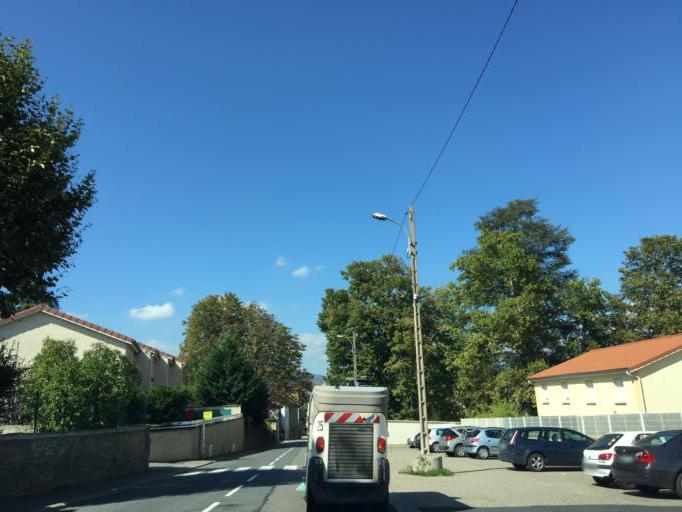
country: FR
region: Rhone-Alpes
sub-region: Departement de la Loire
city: Saint-Paul-en-Jarez
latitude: 45.4819
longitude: 4.5778
